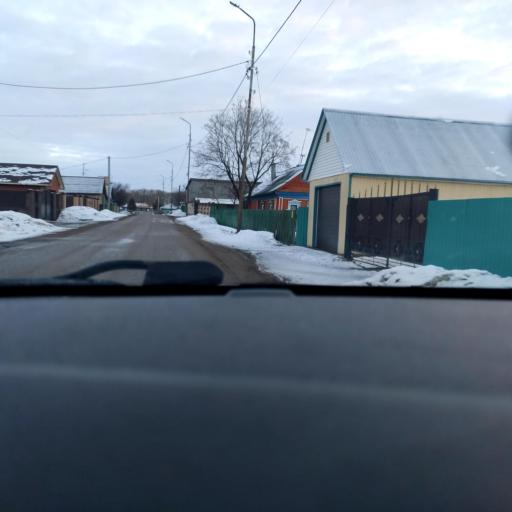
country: RU
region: Bashkortostan
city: Kushnarenkovo
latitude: 55.1012
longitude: 55.3641
